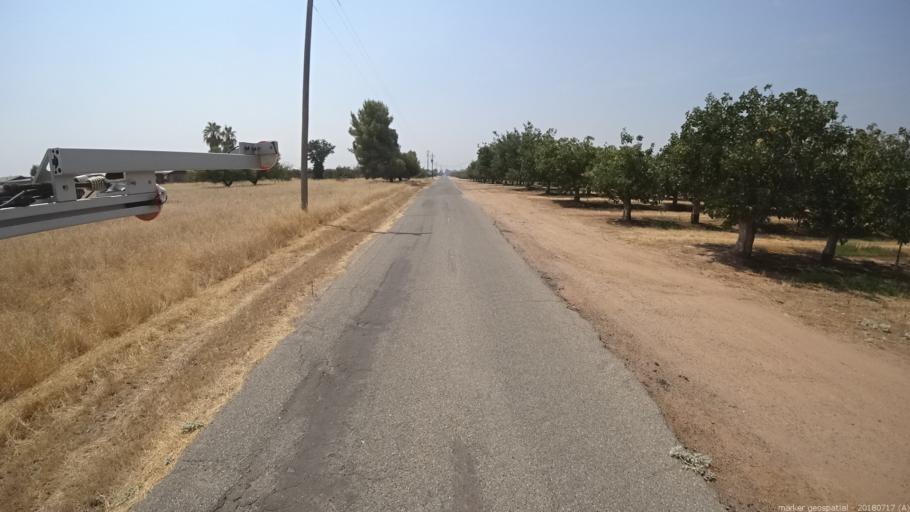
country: US
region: California
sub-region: Madera County
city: Fairmead
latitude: 37.1426
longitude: -120.1382
